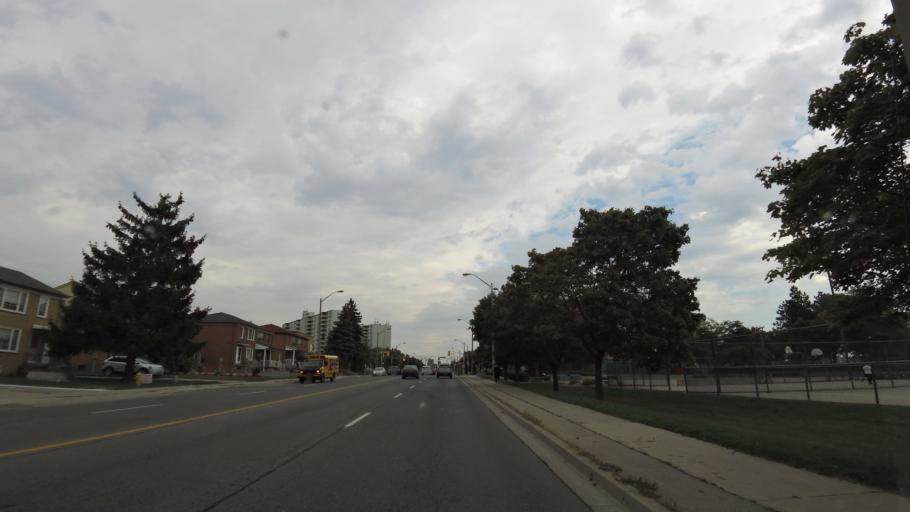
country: CA
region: Ontario
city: Toronto
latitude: 43.7071
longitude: -79.4841
